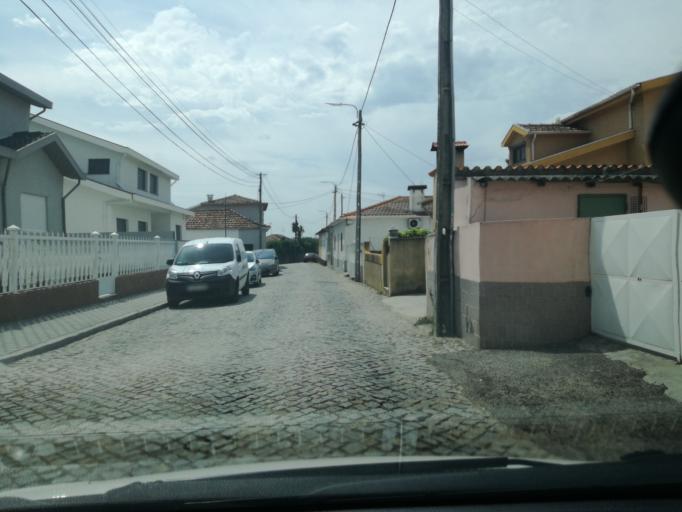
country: PT
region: Porto
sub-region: Vila Nova de Gaia
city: Grijo
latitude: 41.0271
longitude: -8.5894
